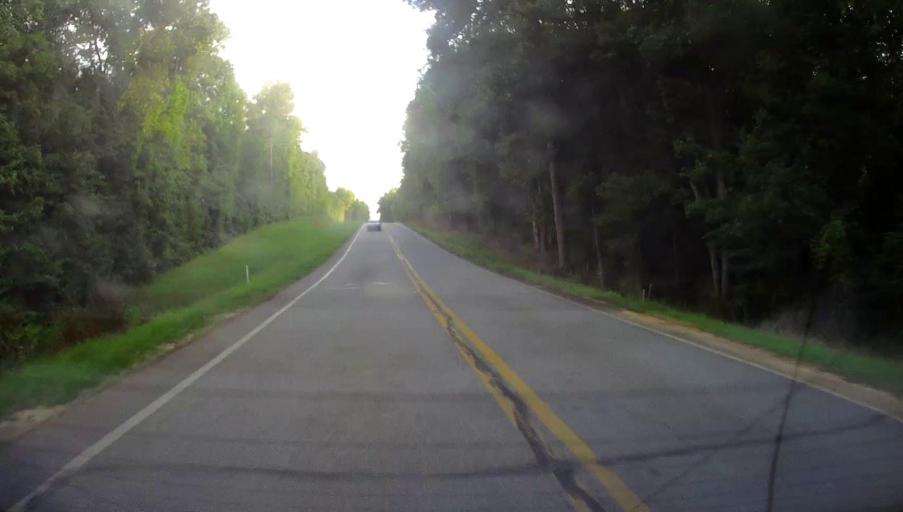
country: US
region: Georgia
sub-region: Crawford County
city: Knoxville
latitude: 32.8575
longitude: -83.9999
